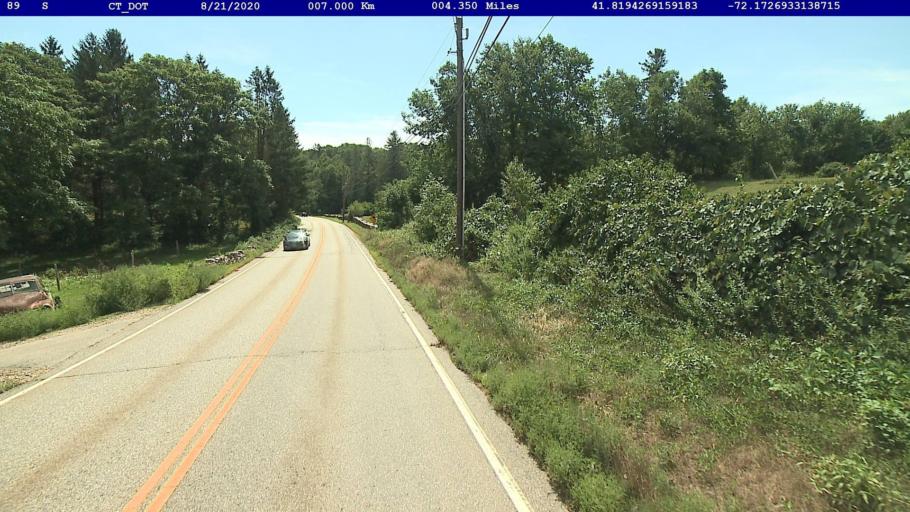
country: US
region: Connecticut
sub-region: Tolland County
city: Storrs
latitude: 41.8194
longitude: -72.1726
